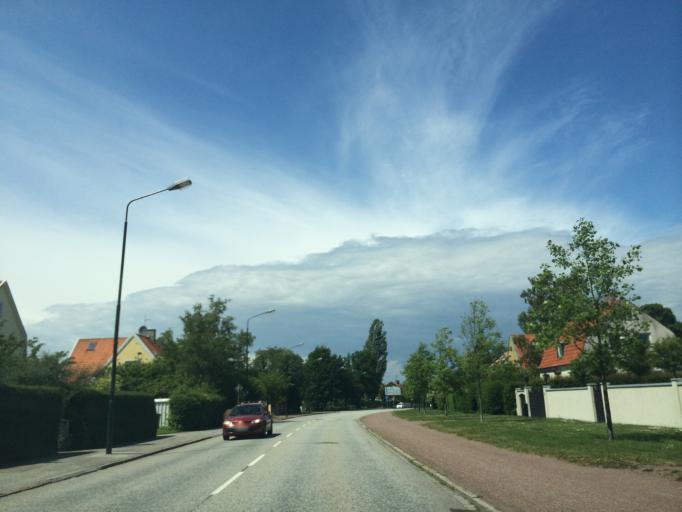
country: SE
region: Skane
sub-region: Malmo
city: Malmoe
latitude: 55.5872
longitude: 12.9667
